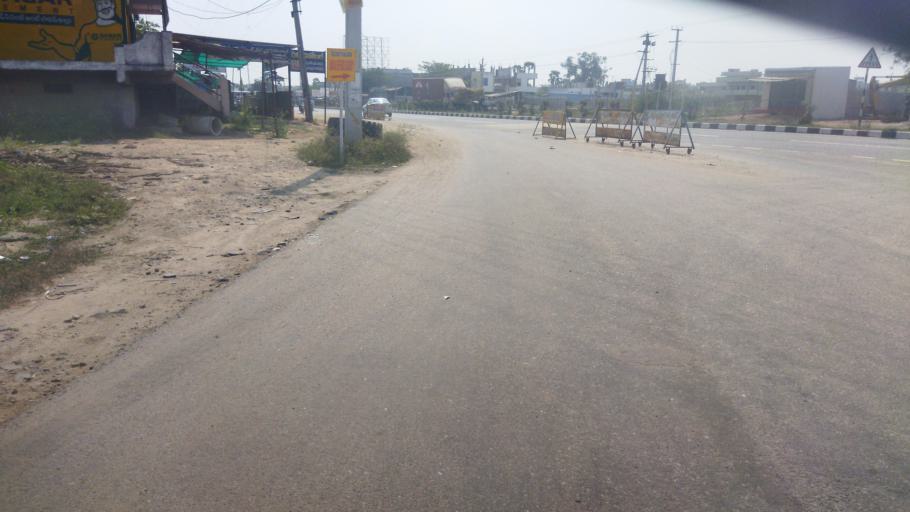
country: IN
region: Telangana
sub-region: Nalgonda
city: Nalgonda
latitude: 17.0749
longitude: 79.2844
